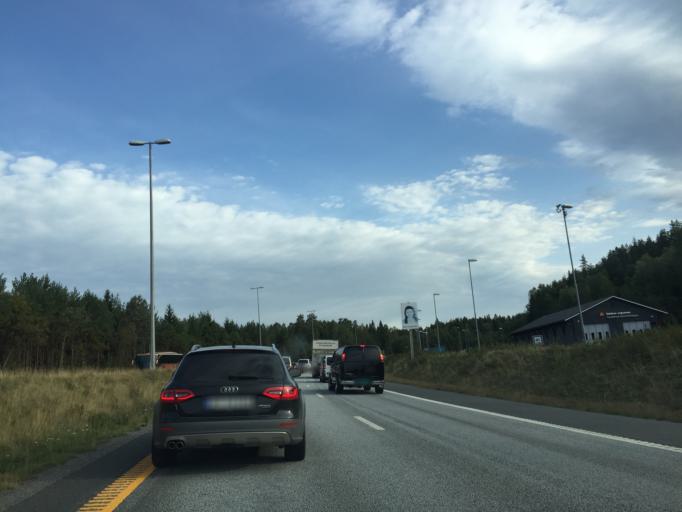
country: NO
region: Akershus
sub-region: Oppegard
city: Kolbotn
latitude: 59.8114
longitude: 10.8399
